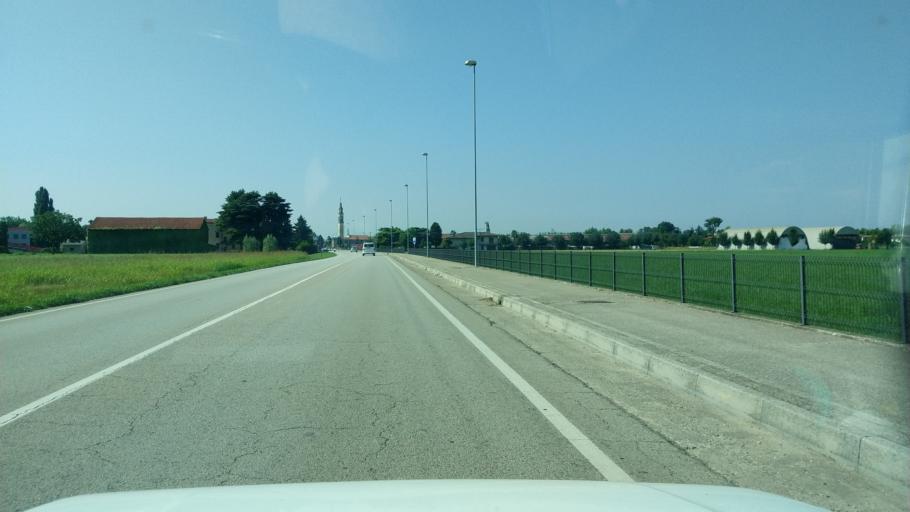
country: IT
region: Veneto
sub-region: Provincia di Vicenza
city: Schiavon
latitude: 45.6888
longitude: 11.6421
